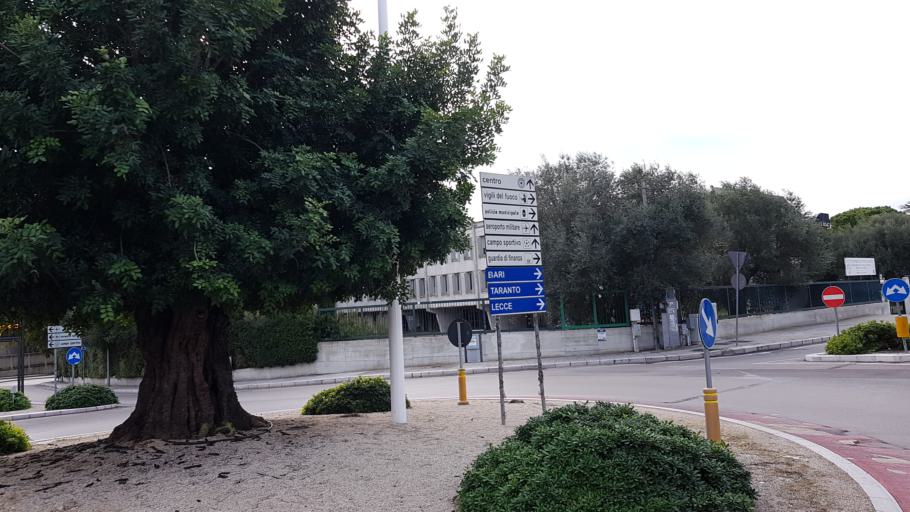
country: IT
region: Apulia
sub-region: Provincia di Brindisi
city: Brindisi
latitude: 40.6446
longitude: 17.9325
